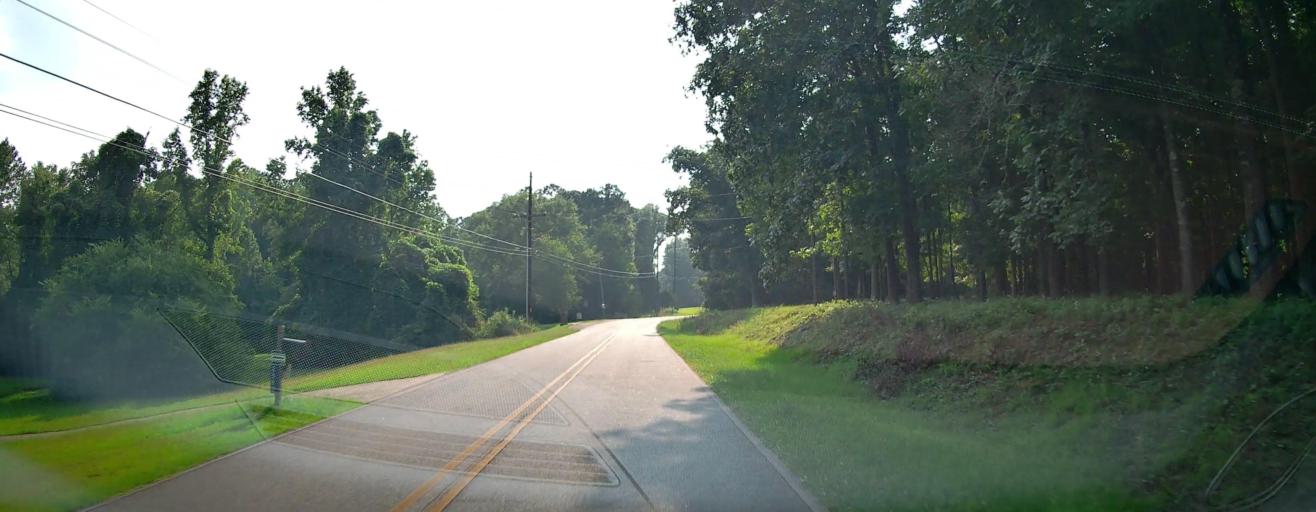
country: US
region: Georgia
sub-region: Bibb County
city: Macon
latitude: 32.9450
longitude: -83.7293
